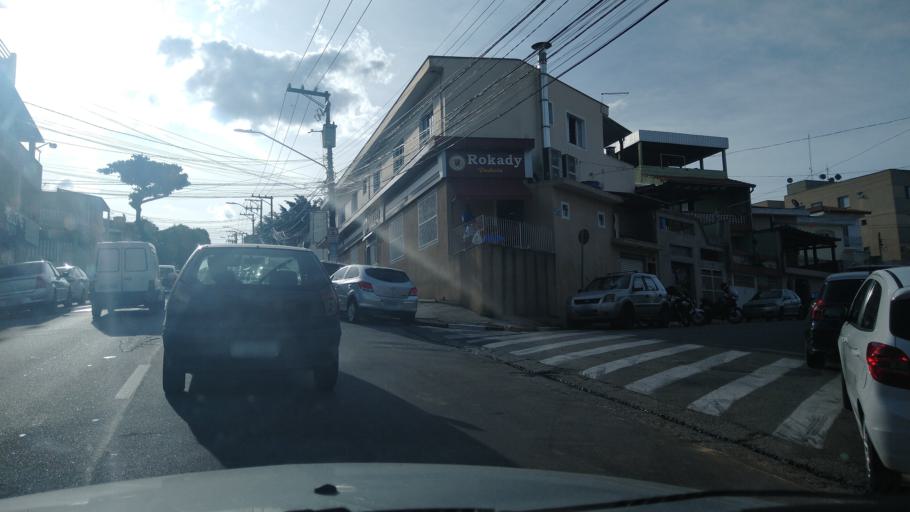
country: BR
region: Sao Paulo
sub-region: Osasco
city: Osasco
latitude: -23.5320
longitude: -46.8039
